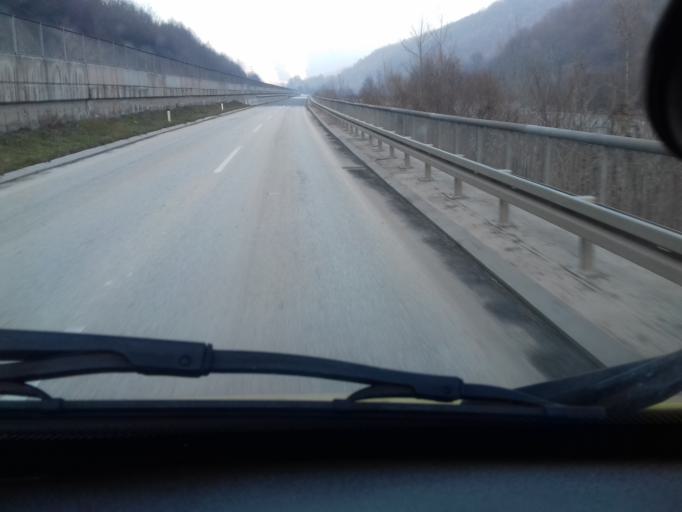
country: BA
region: Federation of Bosnia and Herzegovina
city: Dobrinje
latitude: 44.0641
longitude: 18.1044
